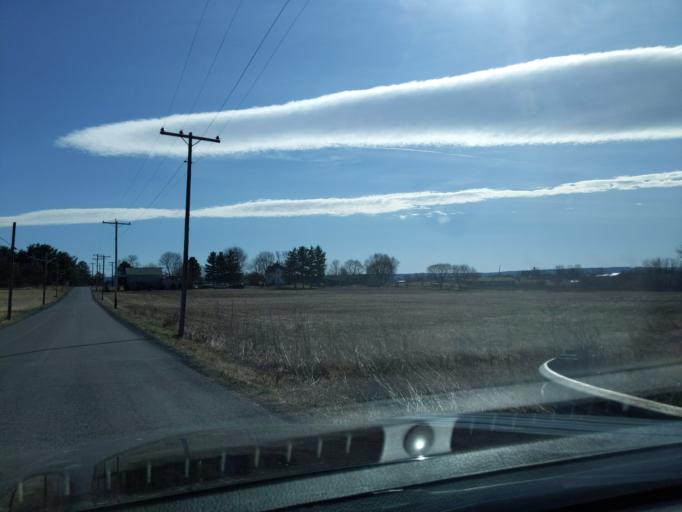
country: US
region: Pennsylvania
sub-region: Blair County
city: Martinsburg
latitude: 40.3119
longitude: -78.3393
